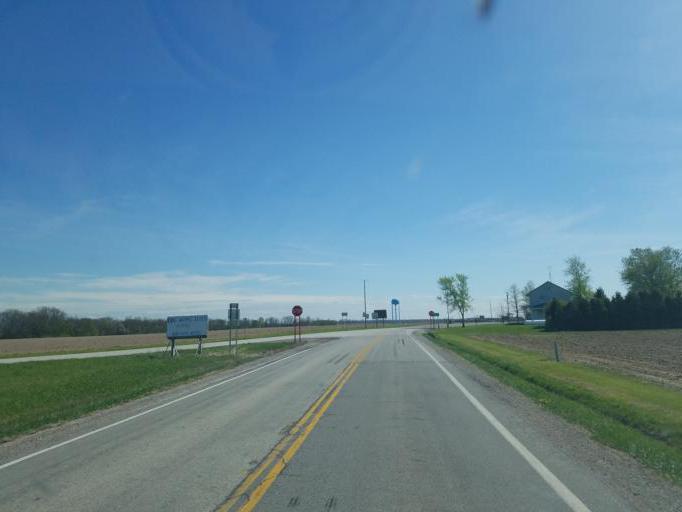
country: US
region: Ohio
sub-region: Huron County
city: Bellevue
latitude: 41.1749
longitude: -82.8367
